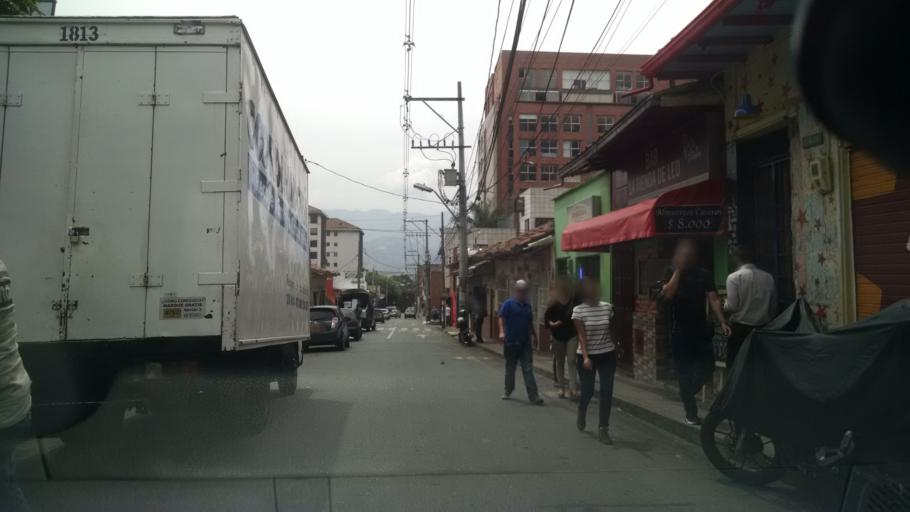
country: CO
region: Antioquia
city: Itagui
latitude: 6.2102
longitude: -75.5717
